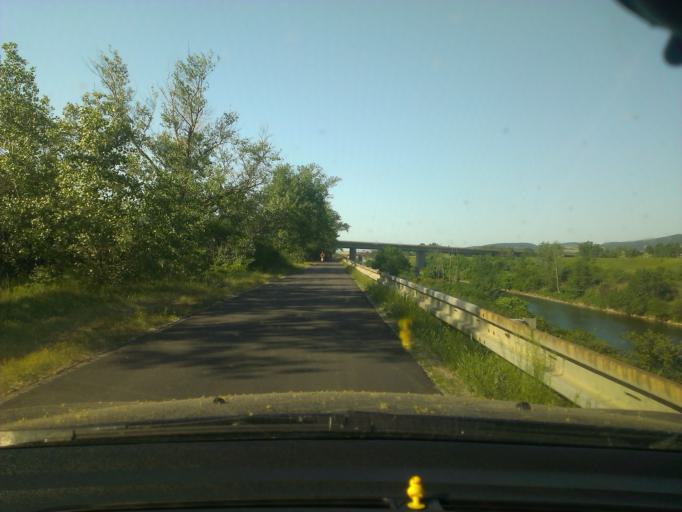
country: SK
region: Trnavsky
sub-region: Okres Trnava
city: Piestany
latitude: 48.6470
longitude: 17.8489
